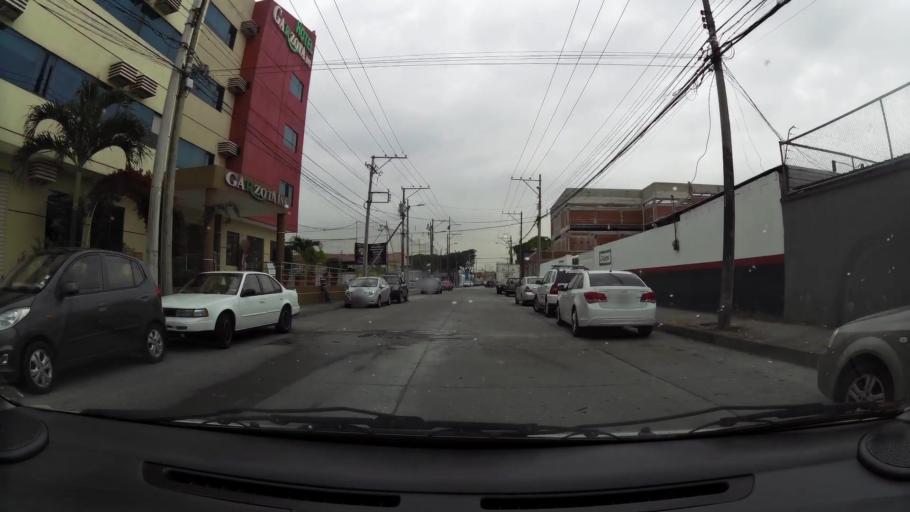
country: EC
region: Guayas
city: Eloy Alfaro
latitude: -2.1465
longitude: -79.8867
